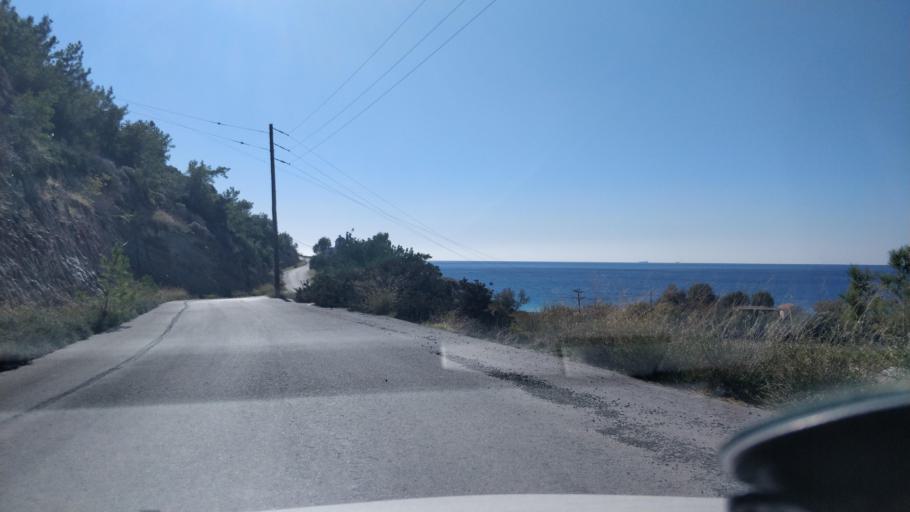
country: GR
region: Crete
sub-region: Nomos Lasithiou
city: Gra Liyia
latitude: 34.9886
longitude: 25.4834
